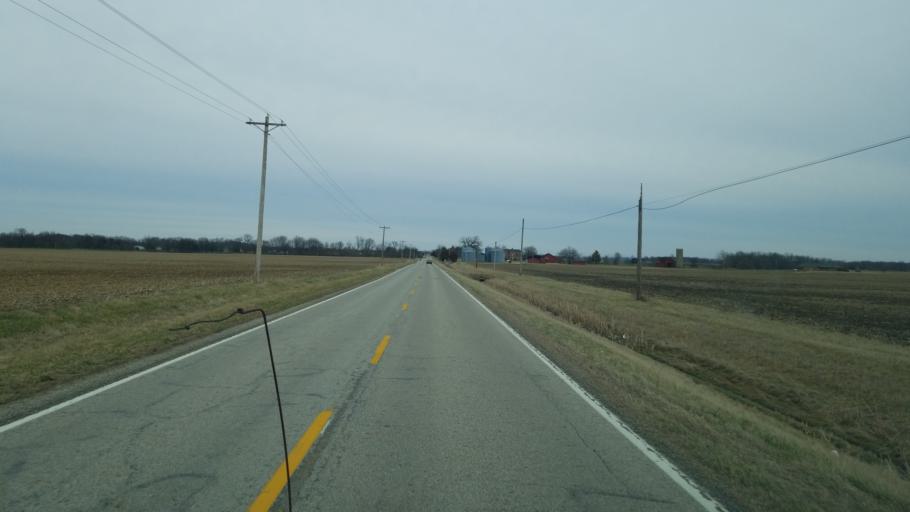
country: US
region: Ohio
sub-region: Pickaway County
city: Williamsport
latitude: 39.5647
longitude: -83.0780
